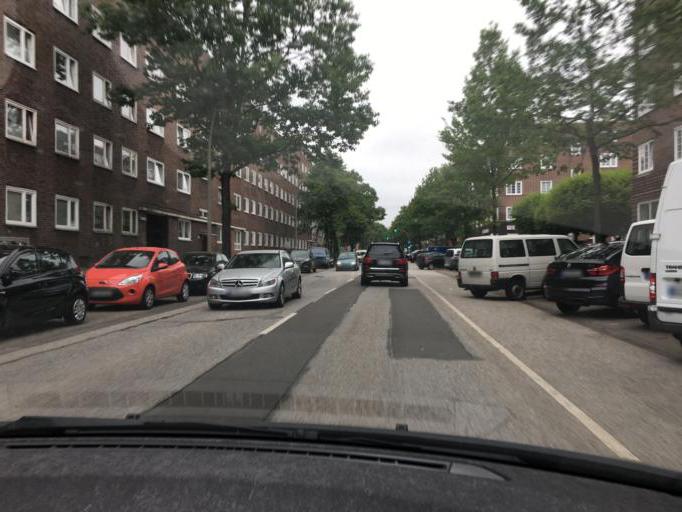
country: DE
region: Hamburg
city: Kleiner Grasbrook
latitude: 53.5142
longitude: 9.9932
